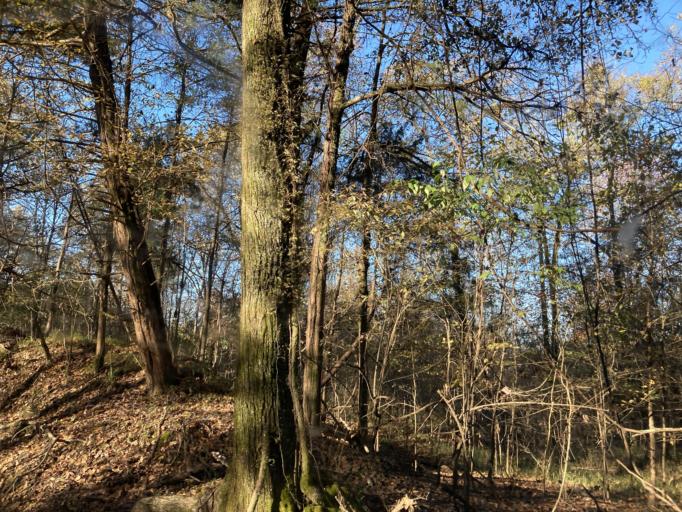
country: US
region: Mississippi
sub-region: Yazoo County
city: Yazoo City
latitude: 32.7245
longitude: -90.5000
